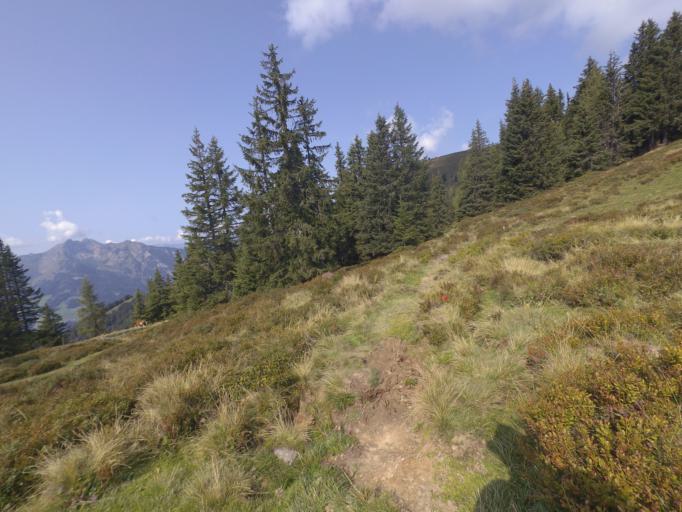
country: AT
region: Salzburg
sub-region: Politischer Bezirk Sankt Johann im Pongau
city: Kleinarl
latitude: 47.2730
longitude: 13.2755
